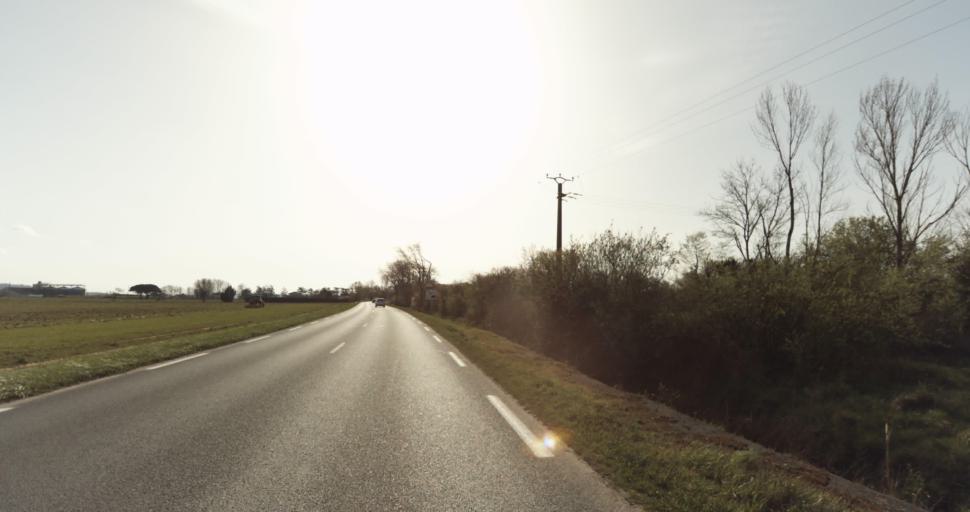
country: FR
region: Midi-Pyrenees
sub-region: Departement du Tarn
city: Saint-Sulpice-la-Pointe
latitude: 43.7522
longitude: 1.7246
